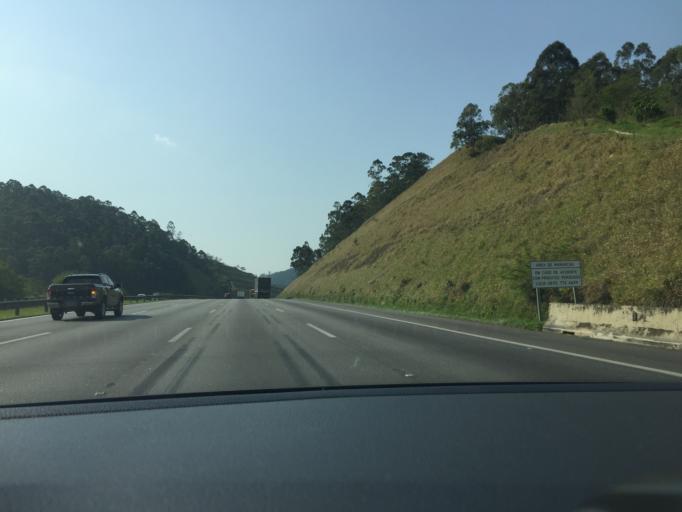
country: BR
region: Sao Paulo
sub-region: Osasco
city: Osasco
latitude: -23.4759
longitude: -46.8017
